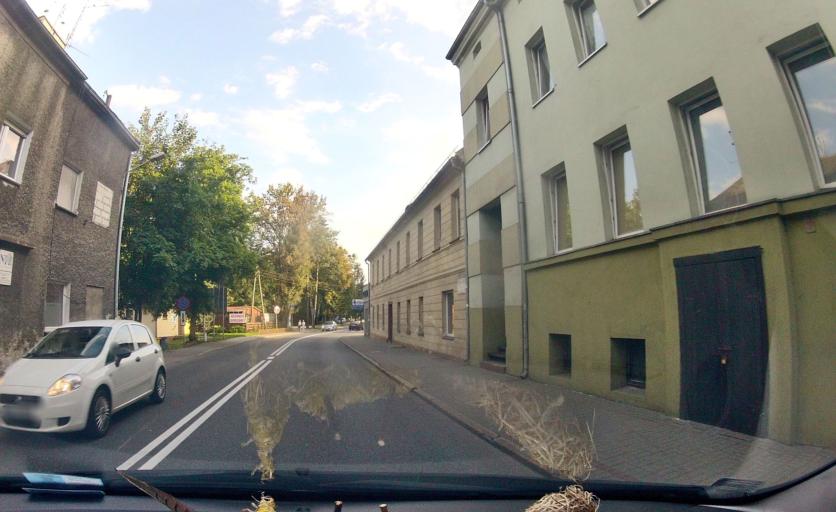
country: PL
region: Opole Voivodeship
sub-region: Powiat kluczborski
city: Kluczbork
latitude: 50.9716
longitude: 18.2181
